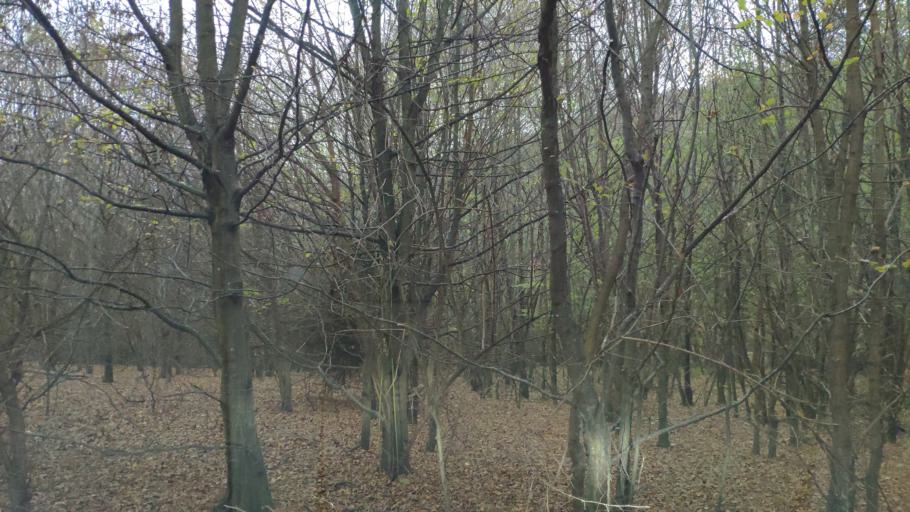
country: SK
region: Presovsky
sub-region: Okres Presov
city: Presov
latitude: 48.9402
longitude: 21.1334
